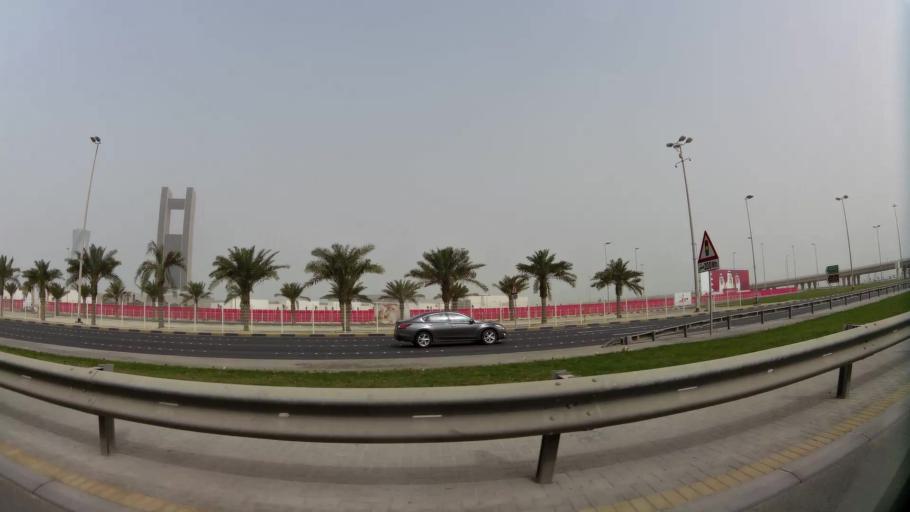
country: BH
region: Muharraq
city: Al Muharraq
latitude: 26.2445
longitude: 50.5881
